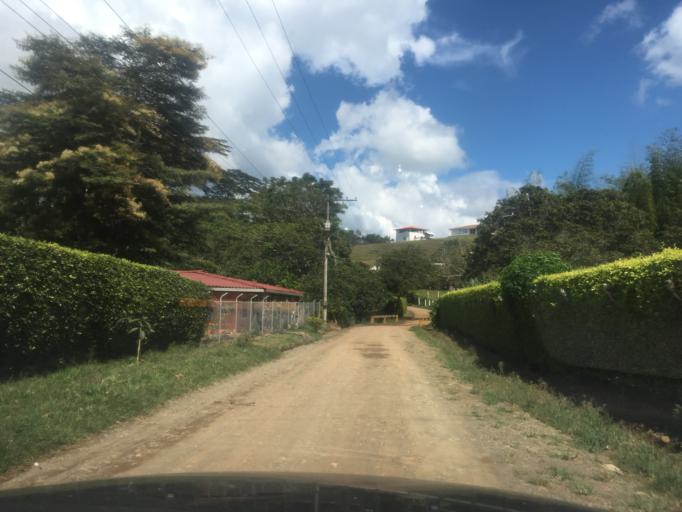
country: CO
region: Valle del Cauca
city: Yumbo
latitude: 3.6605
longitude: -76.5557
